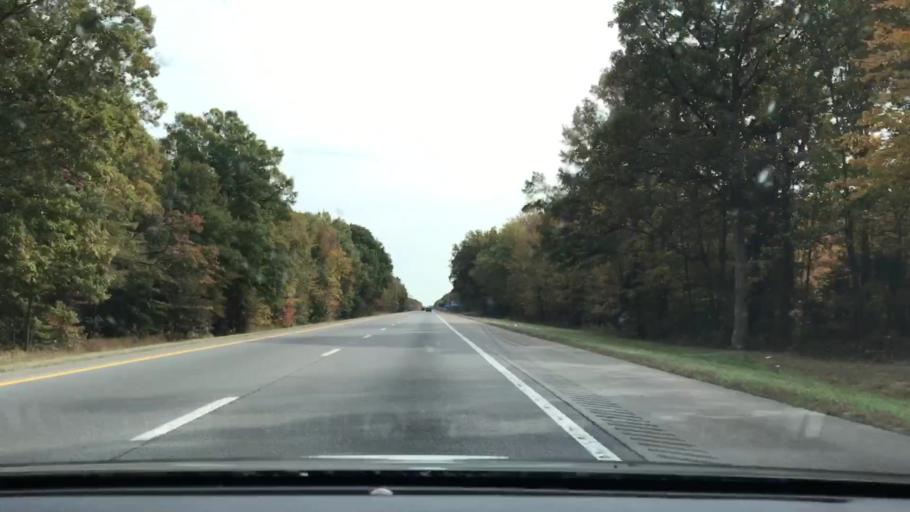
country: US
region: Tennessee
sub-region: Cheatham County
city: Pleasant View
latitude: 36.4185
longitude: -87.0522
